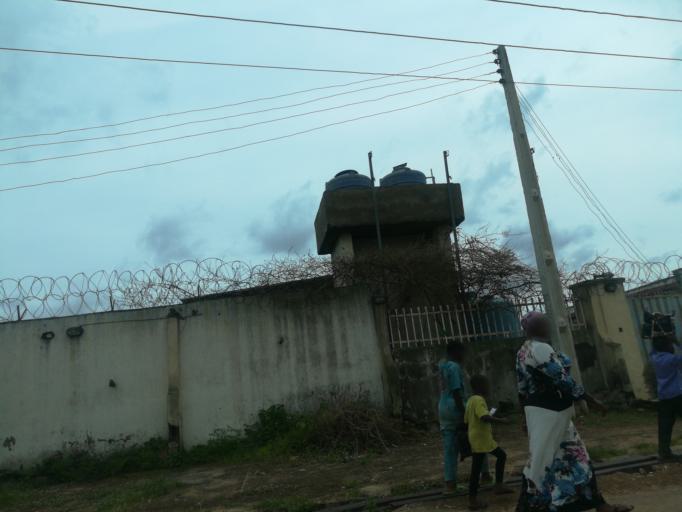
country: NG
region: Oyo
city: Ibadan
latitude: 7.3740
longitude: 3.9694
